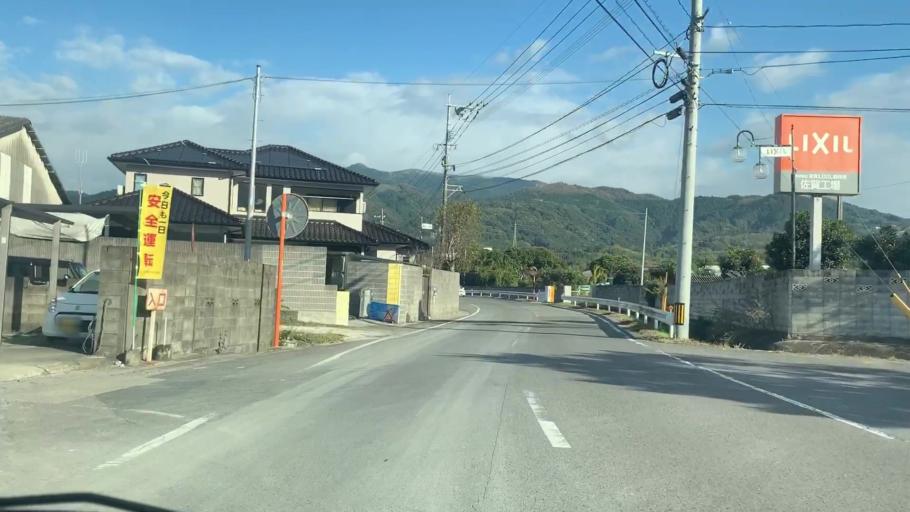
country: JP
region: Saga Prefecture
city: Takeocho-takeo
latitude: 33.2790
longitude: 130.1445
